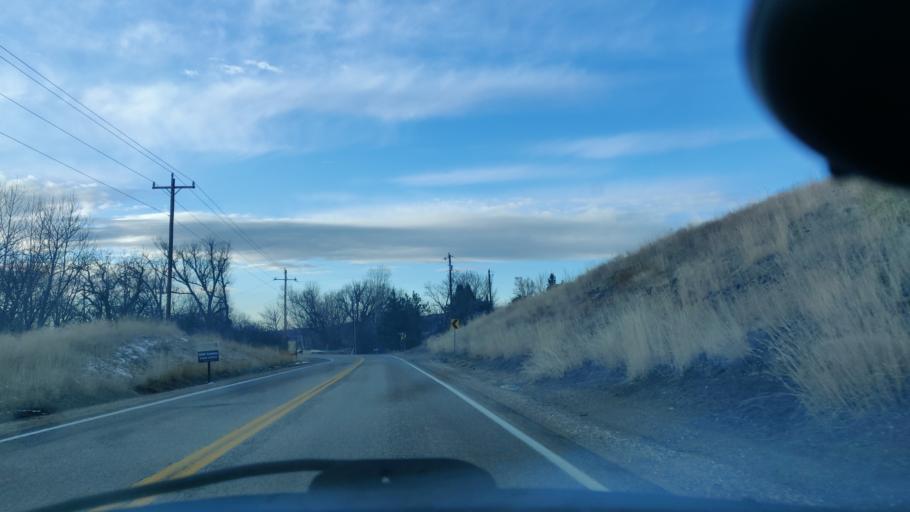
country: US
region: Idaho
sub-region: Ada County
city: Garden City
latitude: 43.7274
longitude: -116.2519
